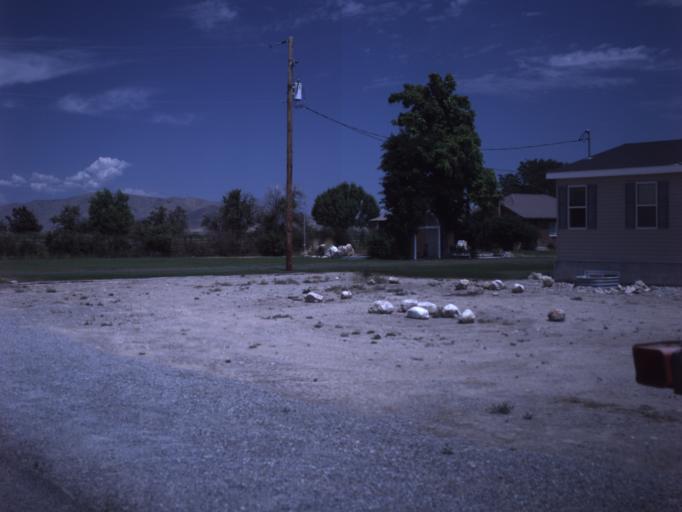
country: US
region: Utah
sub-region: Box Elder County
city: Tremonton
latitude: 41.6556
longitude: -112.2959
